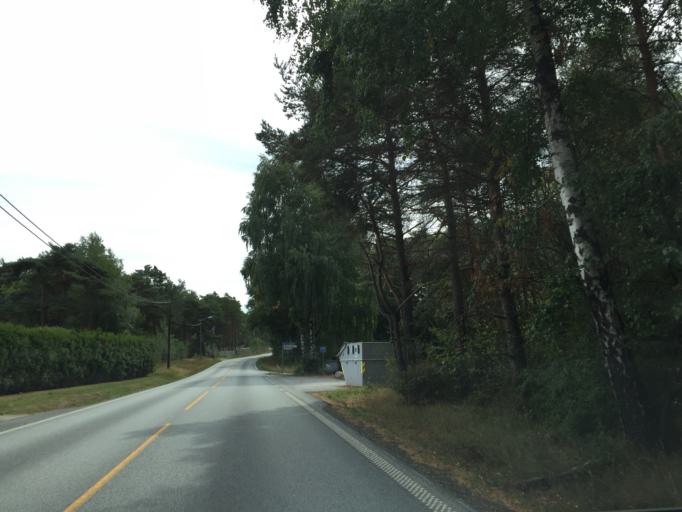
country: NO
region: Ostfold
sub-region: Hvaler
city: Skjaerhalden
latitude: 59.0691
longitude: 10.9340
